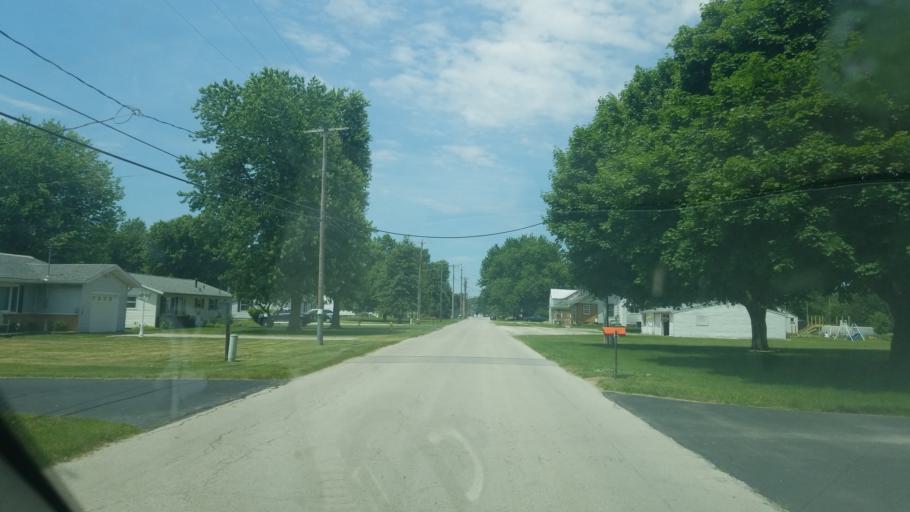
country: US
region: Ohio
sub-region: Wood County
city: North Baltimore
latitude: 41.2537
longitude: -83.5985
